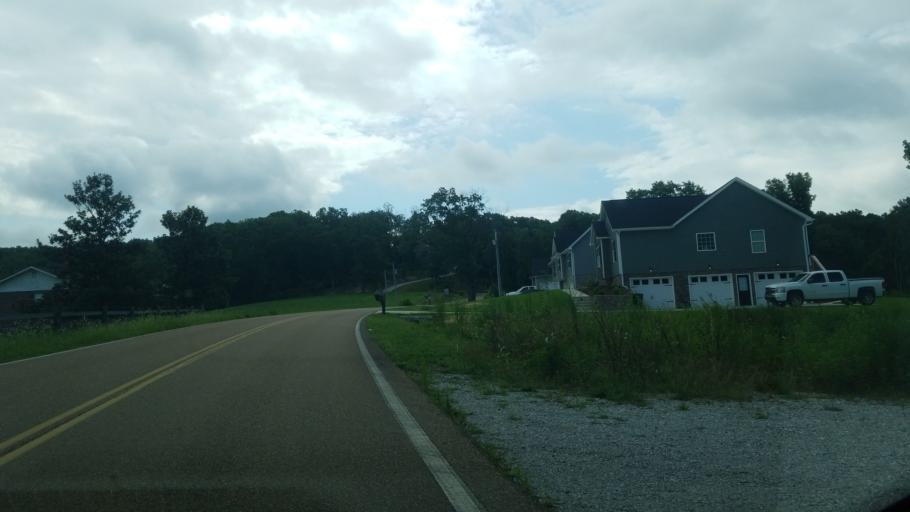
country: US
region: Tennessee
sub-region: Hamilton County
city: Lakesite
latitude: 35.2086
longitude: -85.0796
